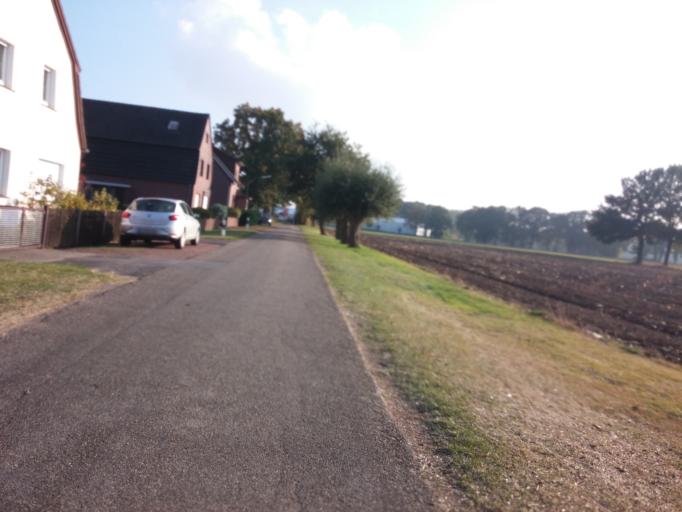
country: DE
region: North Rhine-Westphalia
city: Dorsten
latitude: 51.6393
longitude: 6.9832
